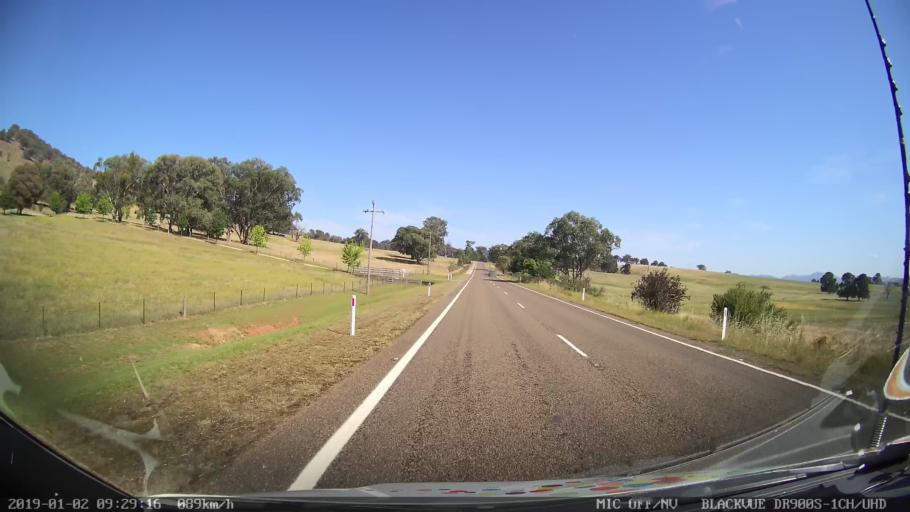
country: AU
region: New South Wales
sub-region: Tumut Shire
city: Tumut
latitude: -35.3405
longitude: 148.2441
